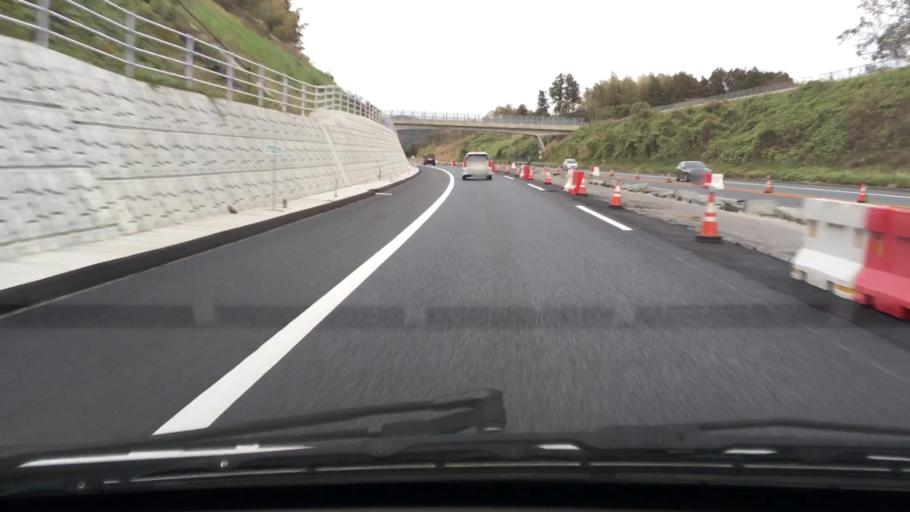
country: JP
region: Chiba
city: Kimitsu
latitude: 35.3006
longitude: 139.9393
